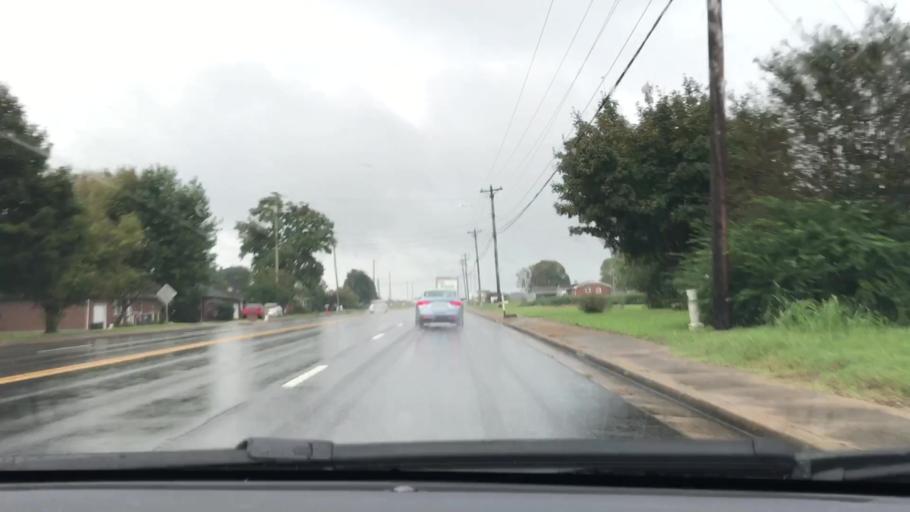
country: US
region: Tennessee
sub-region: Macon County
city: Lafayette
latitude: 36.5274
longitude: -86.0457
